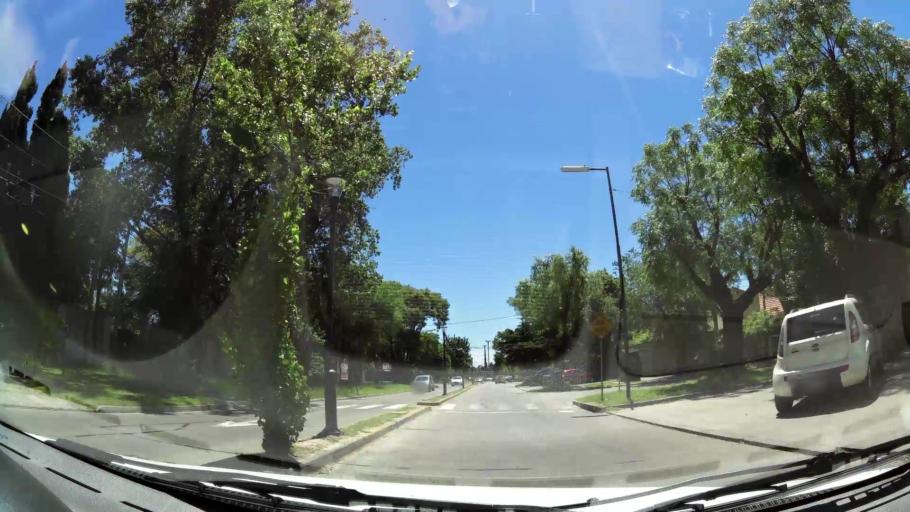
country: AR
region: Buenos Aires
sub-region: Partido de San Isidro
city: San Isidro
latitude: -34.4962
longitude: -58.5590
